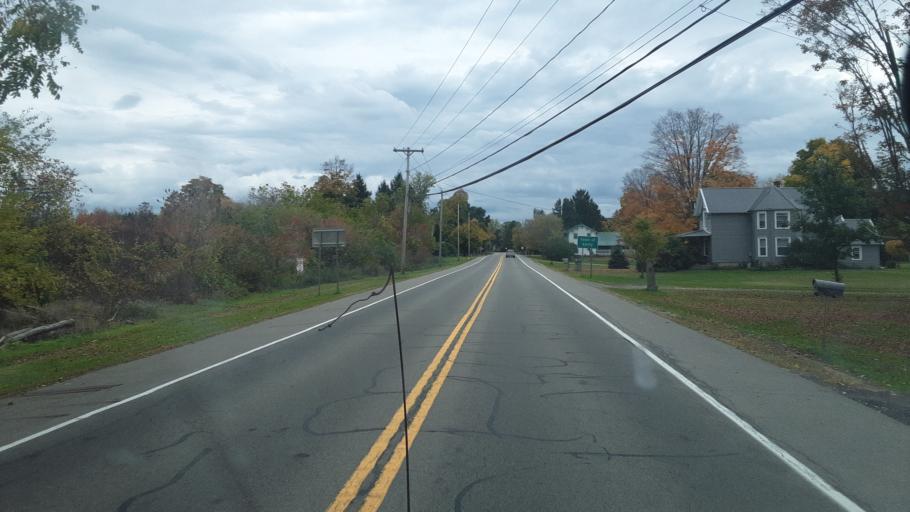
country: US
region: New York
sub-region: Allegany County
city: Belmont
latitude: 42.2179
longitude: -78.0225
